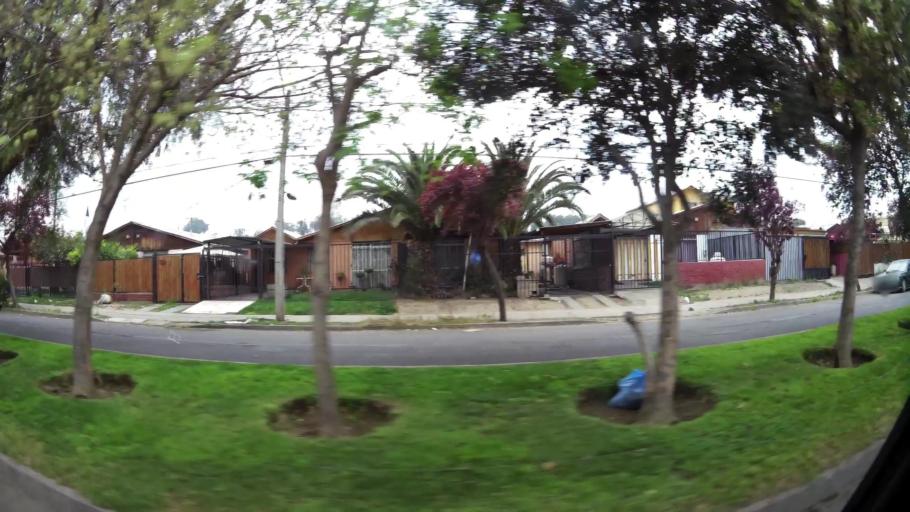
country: CL
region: Santiago Metropolitan
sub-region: Provincia de Santiago
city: Lo Prado
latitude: -33.4878
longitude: -70.7344
